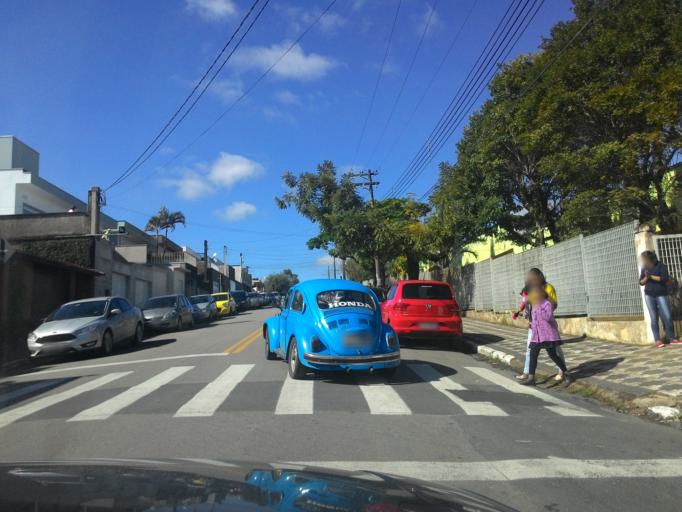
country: BR
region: Sao Paulo
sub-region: Registro
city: Registro
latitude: -24.4992
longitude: -47.8387
